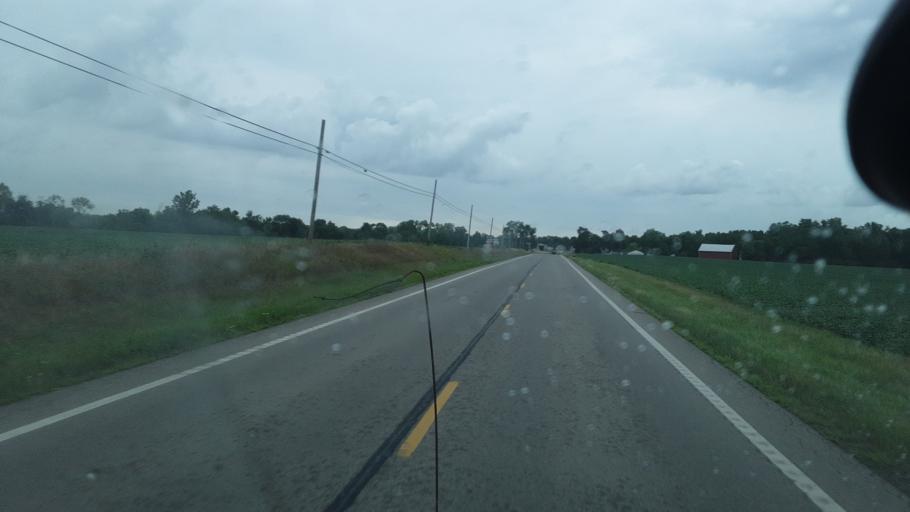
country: US
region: Ohio
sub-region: Williams County
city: Bryan
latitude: 41.4372
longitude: -84.6018
